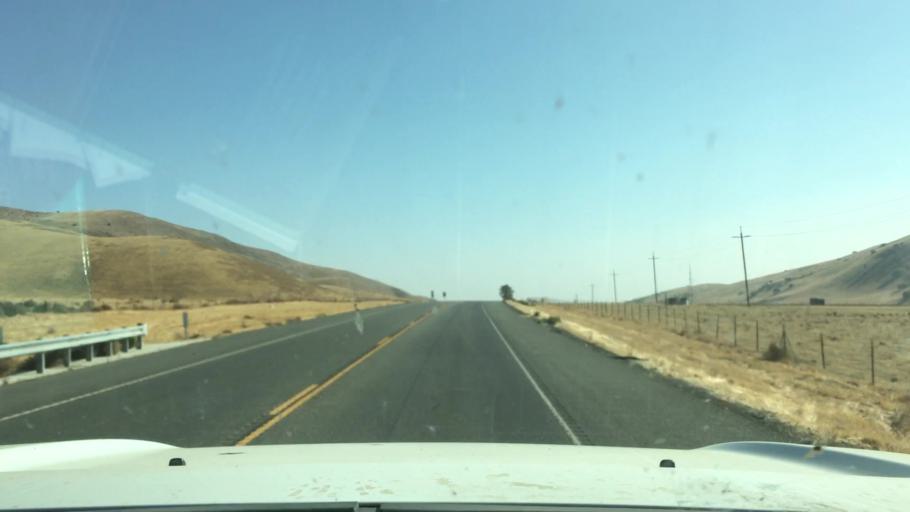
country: US
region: California
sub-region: San Luis Obispo County
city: Shandon
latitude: 35.7283
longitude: -120.1980
